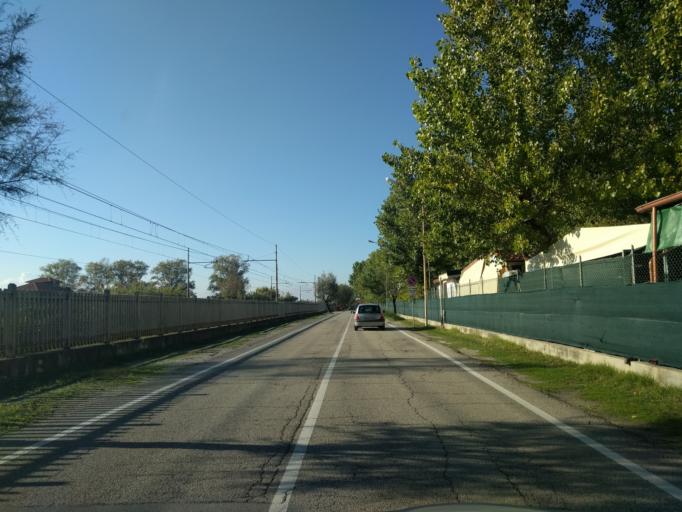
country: IT
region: The Marches
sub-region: Provincia di Pesaro e Urbino
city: Marotta
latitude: 43.7978
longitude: 13.0963
